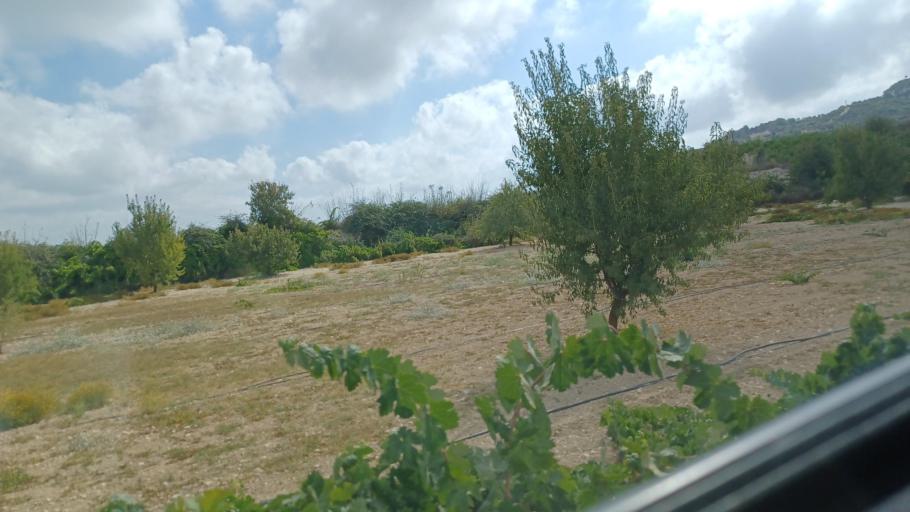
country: CY
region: Pafos
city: Tala
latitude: 34.8672
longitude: 32.4592
